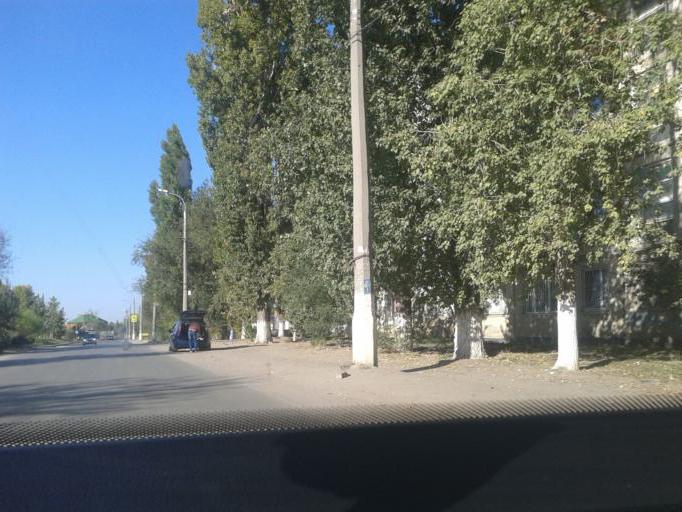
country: RU
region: Volgograd
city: Gorodishche
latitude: 48.7690
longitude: 44.4974
